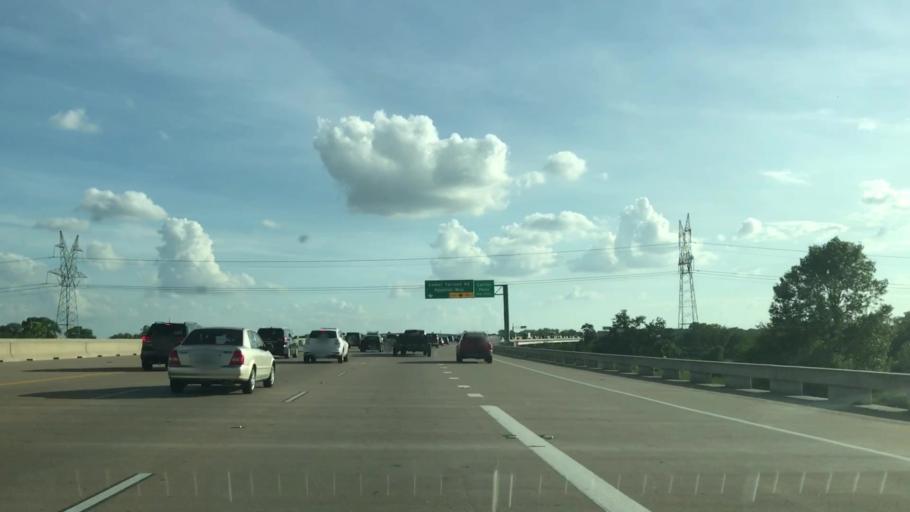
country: US
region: Texas
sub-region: Dallas County
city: Grand Prairie
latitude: 32.7880
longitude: -97.0194
